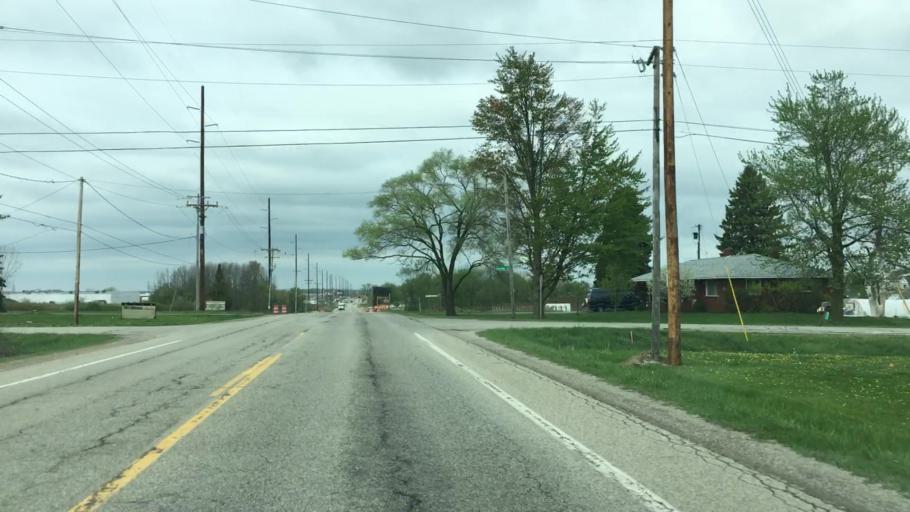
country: US
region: Michigan
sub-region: Ottawa County
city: Hudsonville
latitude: 42.8328
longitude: -85.8618
